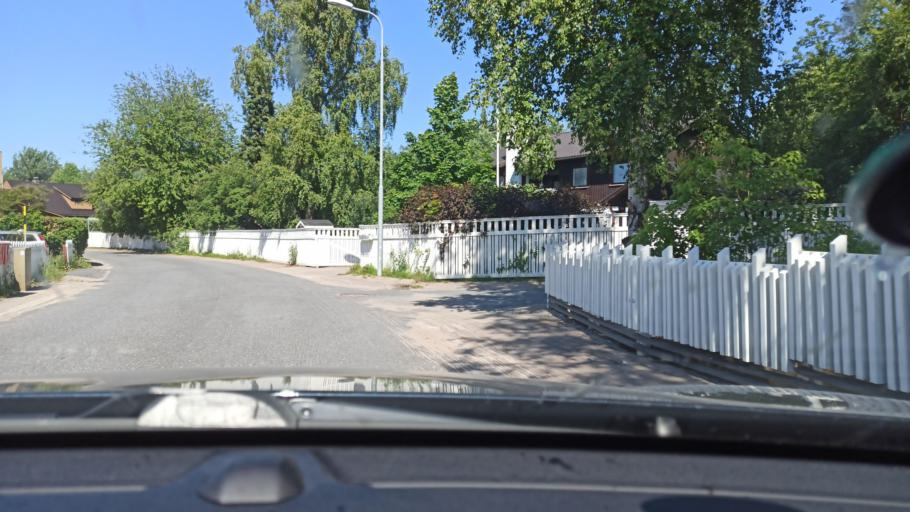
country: FI
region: Northern Ostrobothnia
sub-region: Oulu
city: Oulu
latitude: 65.0407
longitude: 25.4439
